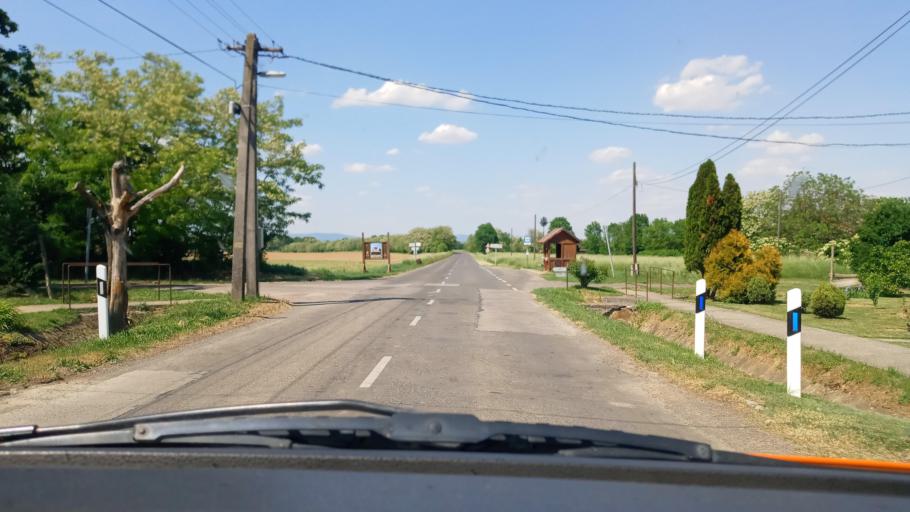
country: HU
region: Baranya
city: Harkany
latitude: 45.8831
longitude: 18.1716
